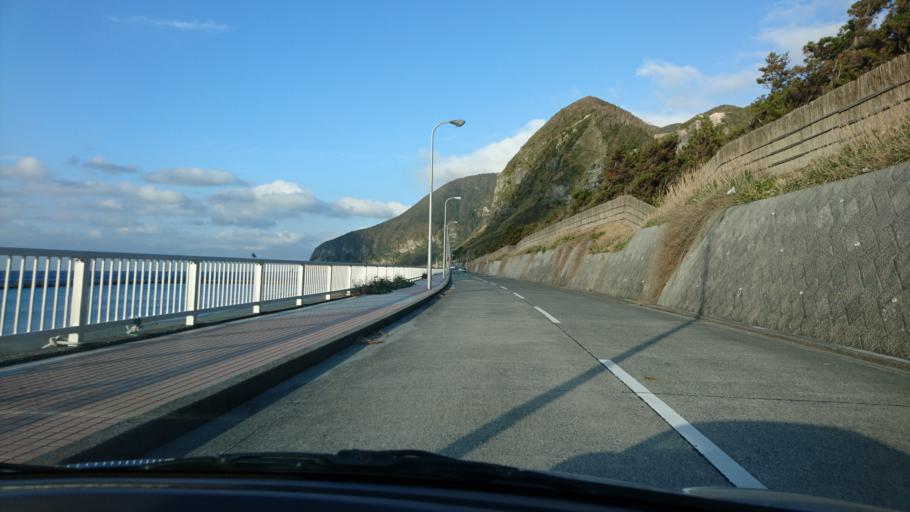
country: JP
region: Shizuoka
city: Shimoda
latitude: 34.3798
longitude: 139.2544
